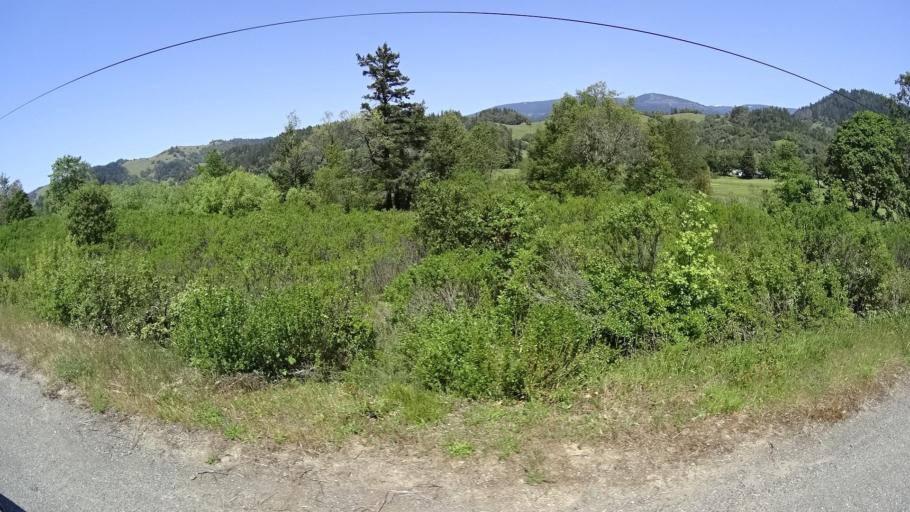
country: US
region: California
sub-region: Humboldt County
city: Redway
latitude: 40.2172
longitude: -123.6422
